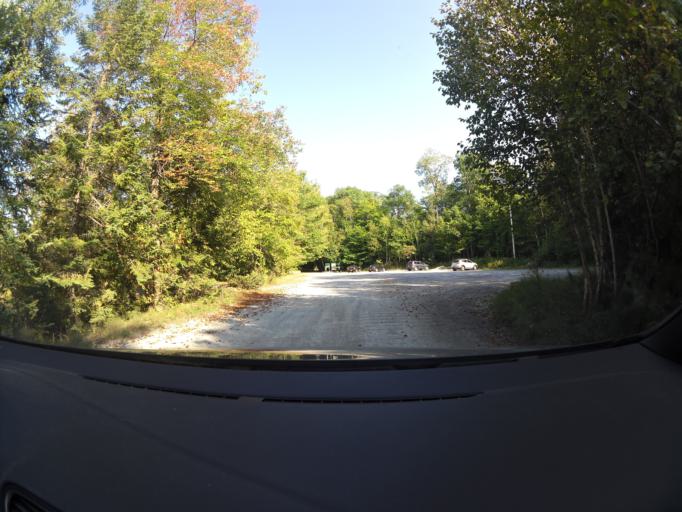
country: CA
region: Ontario
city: Arnprior
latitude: 45.4592
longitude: -76.2717
